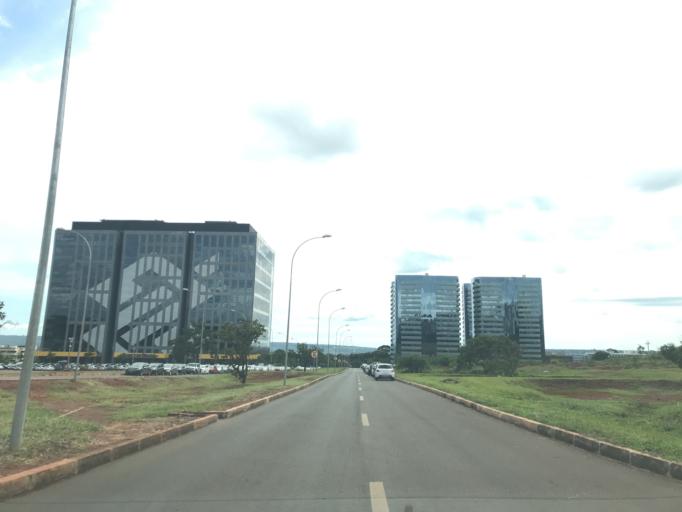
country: BR
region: Federal District
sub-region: Brasilia
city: Brasilia
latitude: -15.7853
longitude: -47.8793
